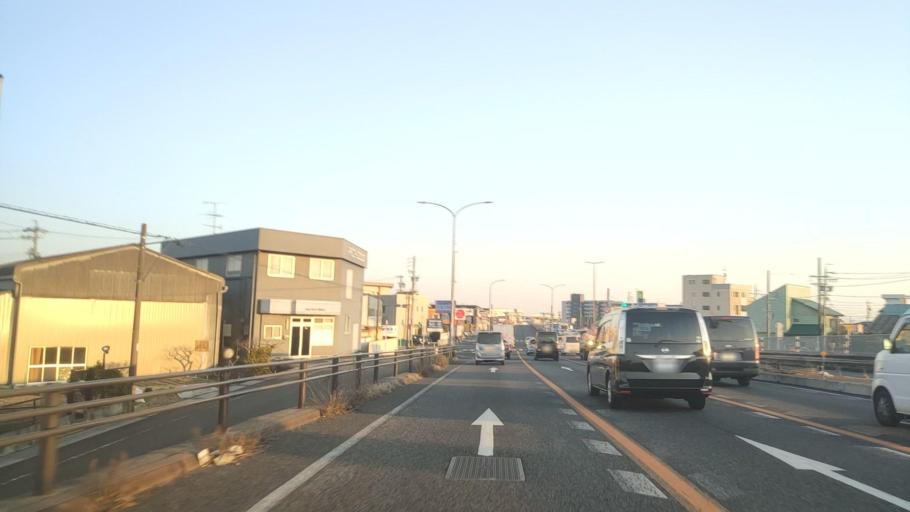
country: JP
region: Aichi
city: Kuroda
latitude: 35.3572
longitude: 136.7859
